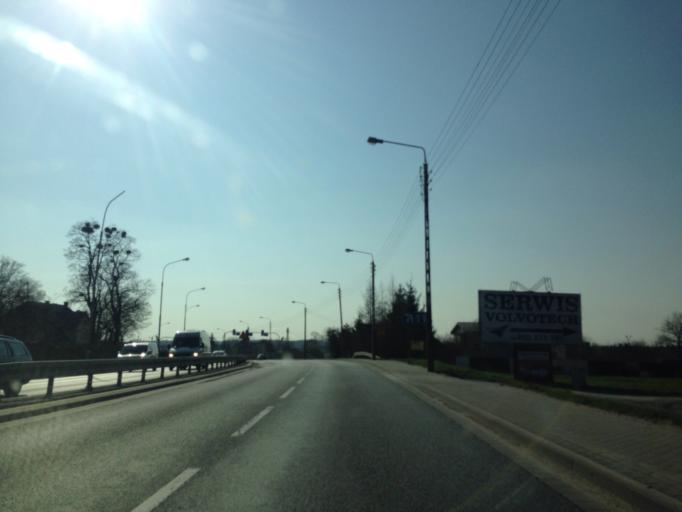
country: PL
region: Lower Silesian Voivodeship
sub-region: Powiat wroclawski
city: Dlugoleka
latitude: 51.1919
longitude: 17.2391
